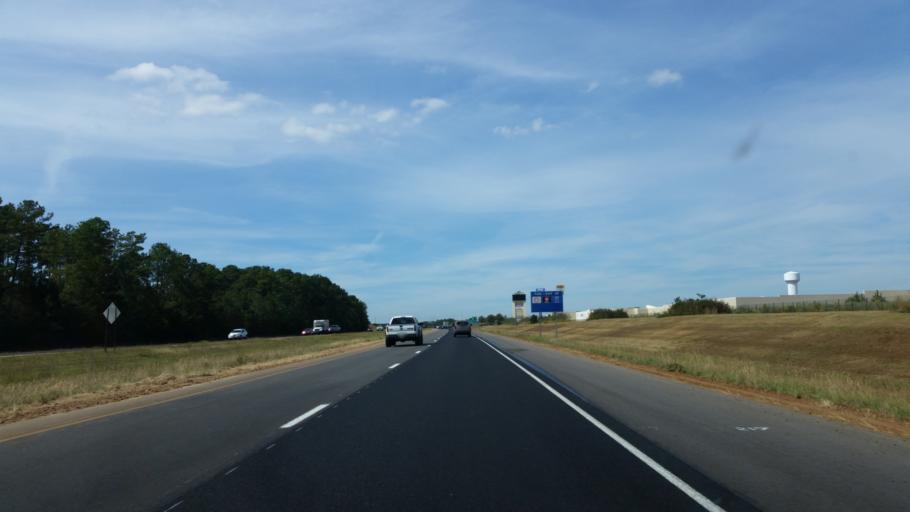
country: US
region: Alabama
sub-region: Baldwin County
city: Spanish Fort
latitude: 30.6630
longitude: -87.8433
